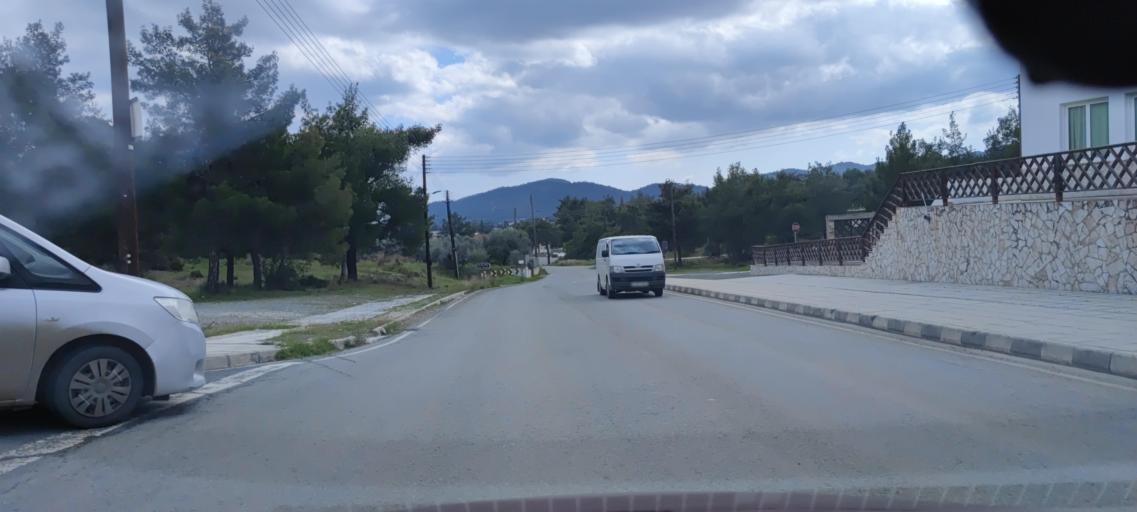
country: CY
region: Lefkosia
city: Lythrodontas
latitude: 34.9620
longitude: 33.2937
